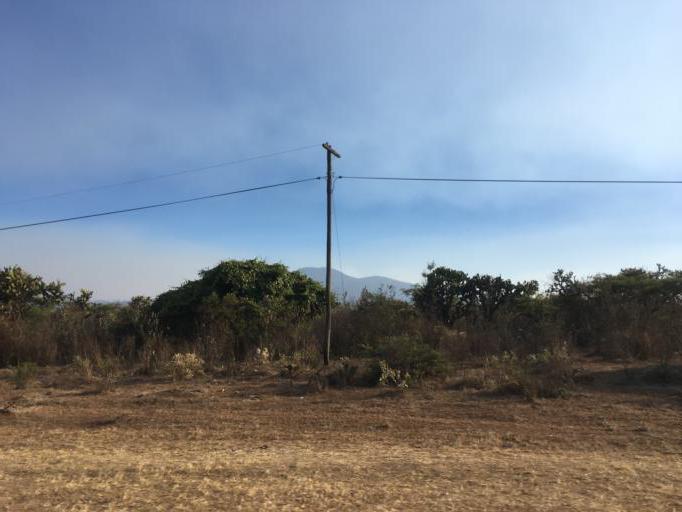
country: MX
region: Michoacan
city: Santa Fe de la Laguna
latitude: 19.6731
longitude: -101.5749
